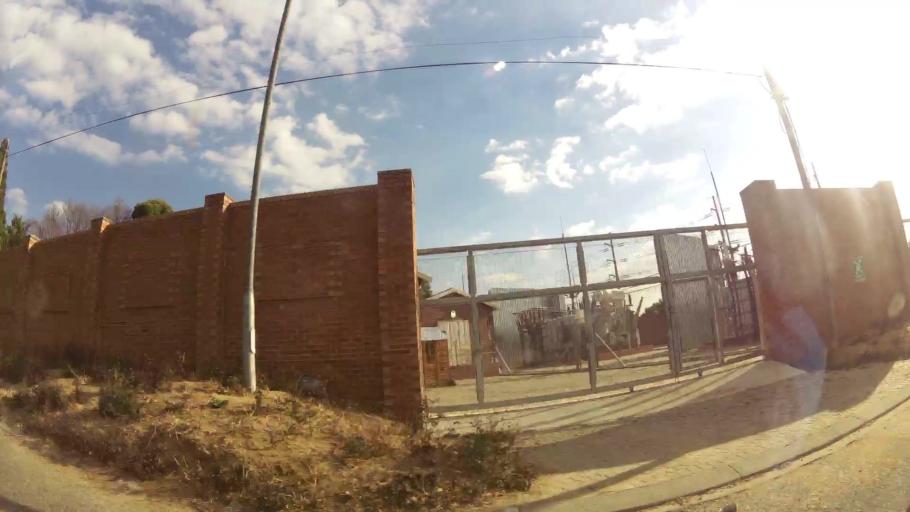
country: ZA
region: Gauteng
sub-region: City of Johannesburg Metropolitan Municipality
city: Diepsloot
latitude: -26.0025
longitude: 28.0264
